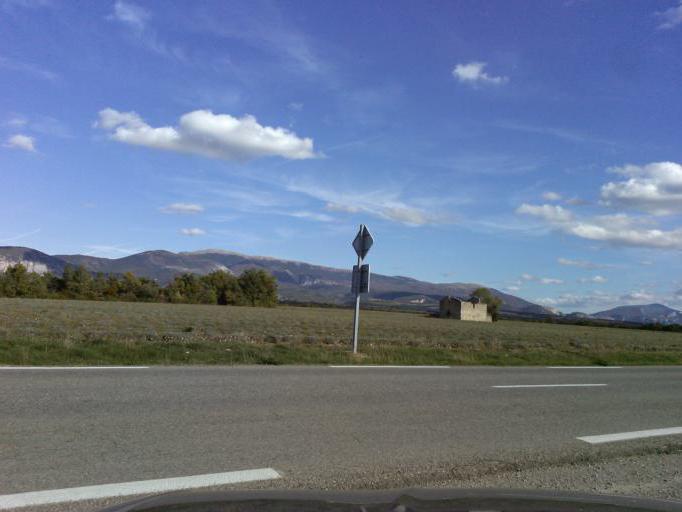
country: FR
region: Provence-Alpes-Cote d'Azur
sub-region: Departement des Alpes-de-Haute-Provence
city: Riez
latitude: 43.8955
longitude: 6.1290
